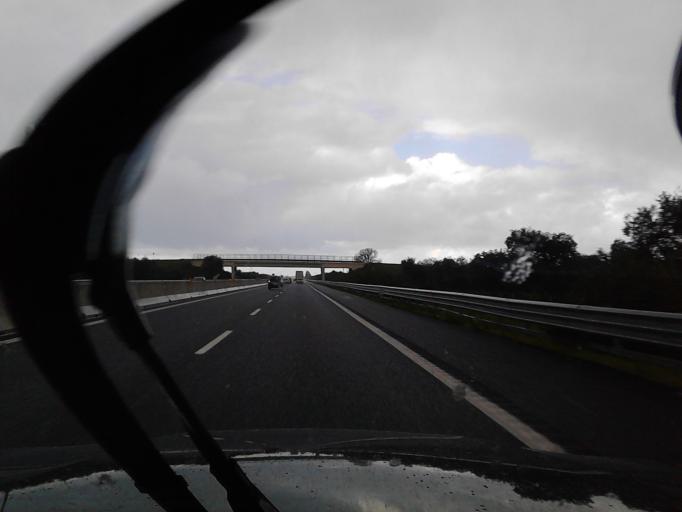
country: IT
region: Apulia
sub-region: Provincia di Bari
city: Giovinazzo
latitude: 41.1594
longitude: 16.6360
